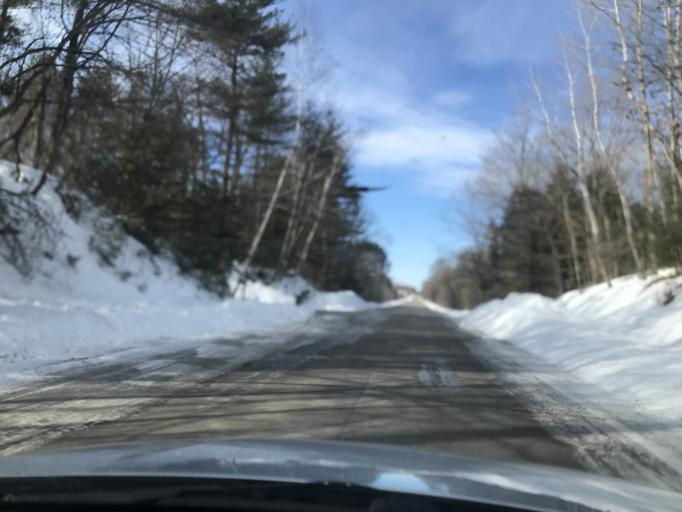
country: US
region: Wisconsin
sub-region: Oconto County
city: Gillett
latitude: 44.9617
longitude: -88.2811
